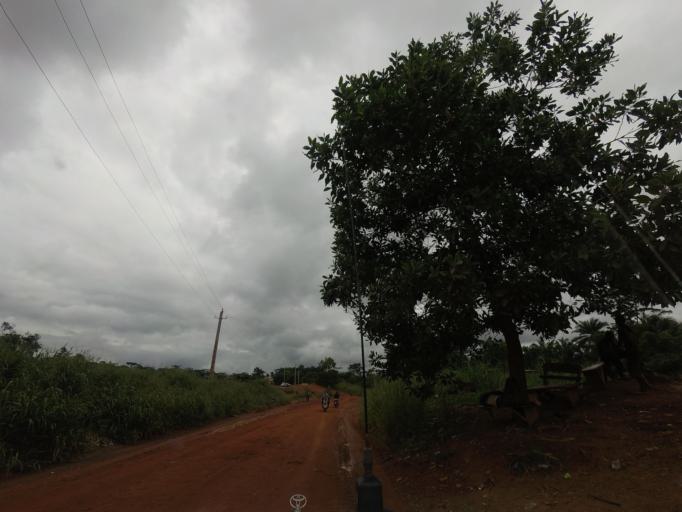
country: LR
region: Nimba
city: Sanniquellie
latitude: 7.3437
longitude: -8.9615
